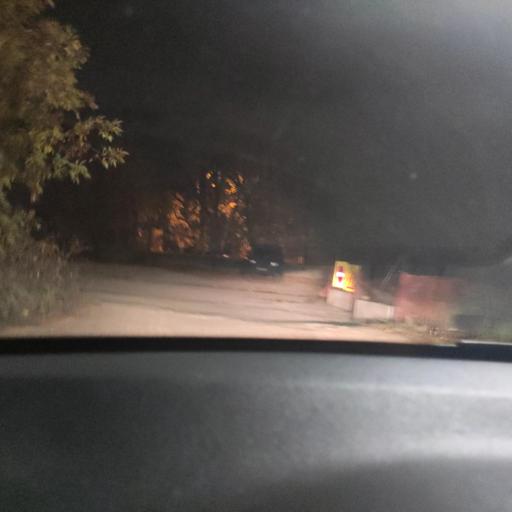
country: RU
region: Samara
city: Samara
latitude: 53.2213
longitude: 50.2238
